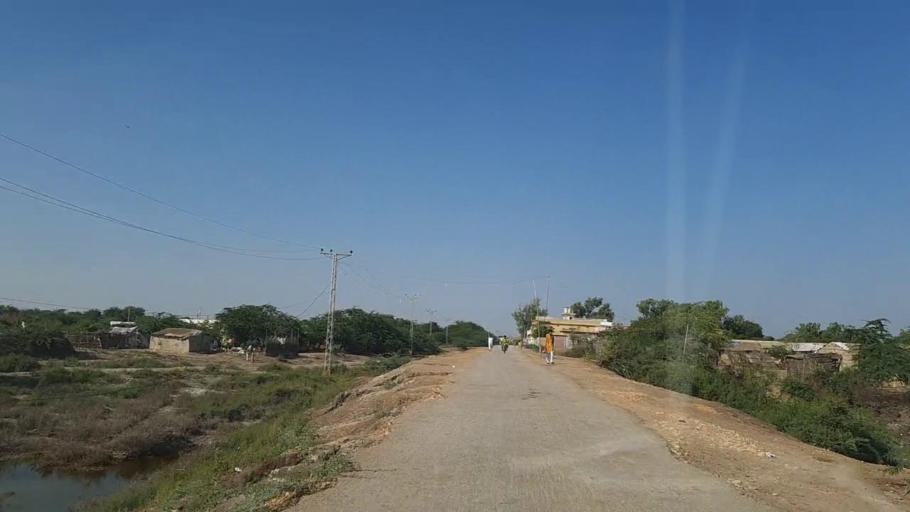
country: PK
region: Sindh
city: Thatta
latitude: 24.6177
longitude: 68.0285
